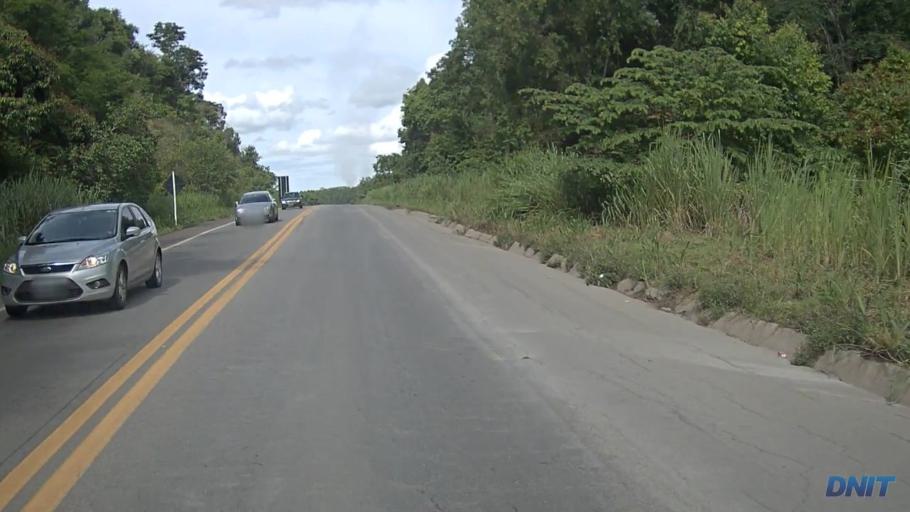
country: BR
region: Minas Gerais
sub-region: Ipaba
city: Ipaba
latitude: -19.3242
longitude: -42.4164
